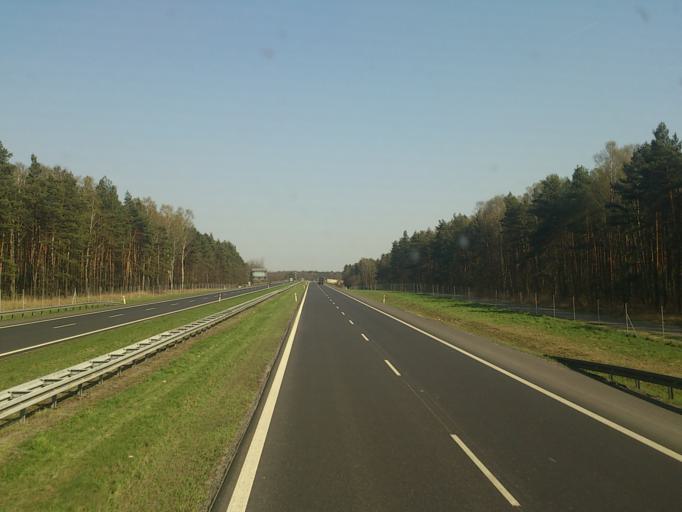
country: PL
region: Lesser Poland Voivodeship
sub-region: Powiat chrzanowski
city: Trzebinia
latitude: 50.1410
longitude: 19.4539
